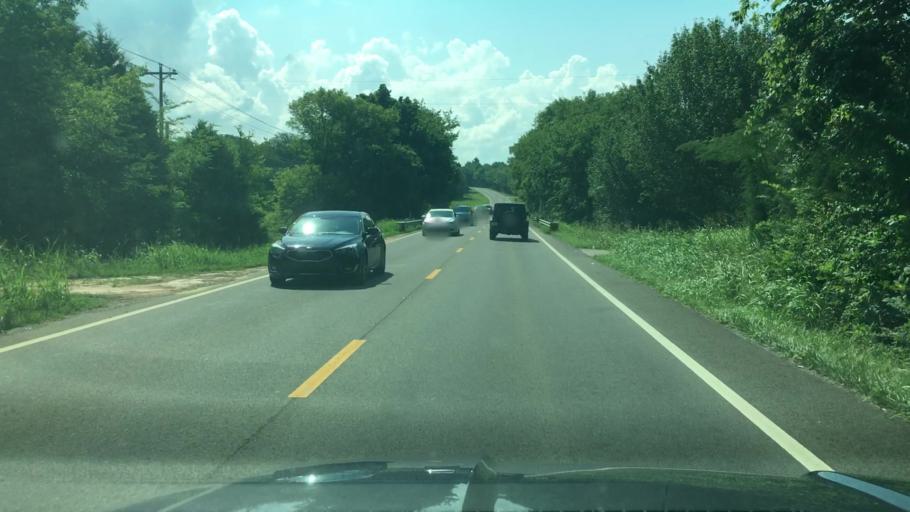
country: US
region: Tennessee
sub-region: Williamson County
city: Nolensville
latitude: 35.8745
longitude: -86.7338
